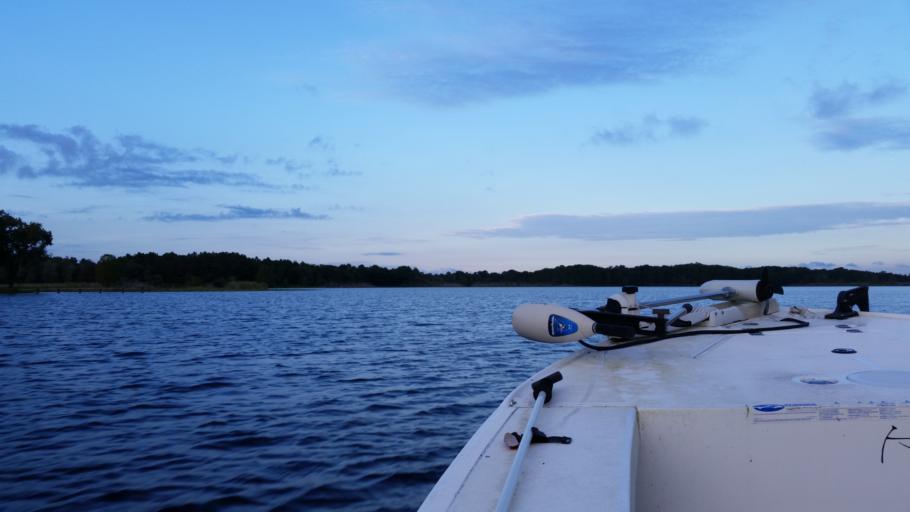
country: US
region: Florida
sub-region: Citrus County
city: Inverness
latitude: 28.8317
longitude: -82.3051
